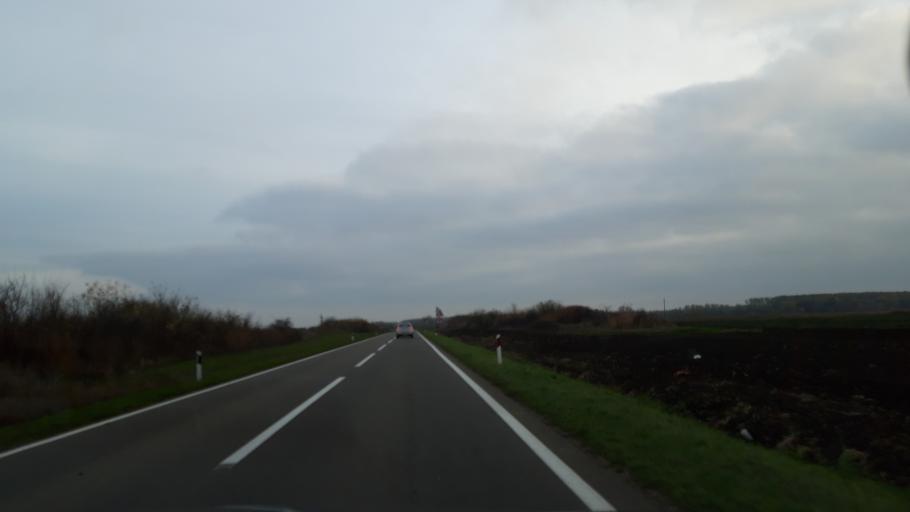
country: RS
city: Sanad
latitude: 46.0024
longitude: 20.1019
